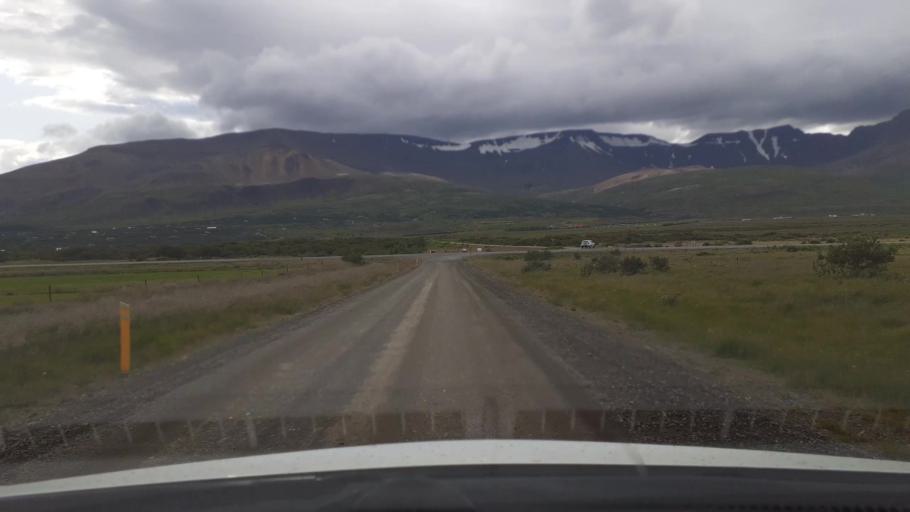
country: IS
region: West
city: Borgarnes
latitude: 64.5444
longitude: -21.6194
